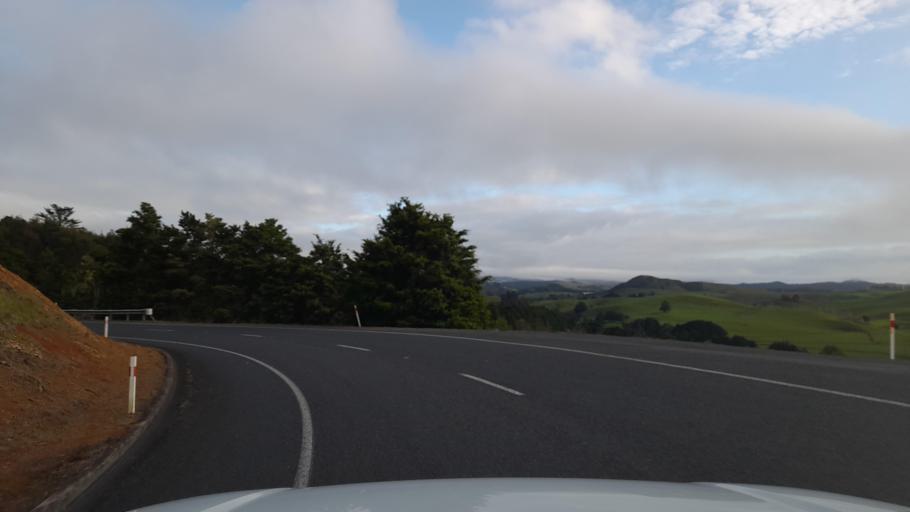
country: NZ
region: Northland
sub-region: Far North District
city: Waimate North
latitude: -35.5106
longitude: 173.8384
